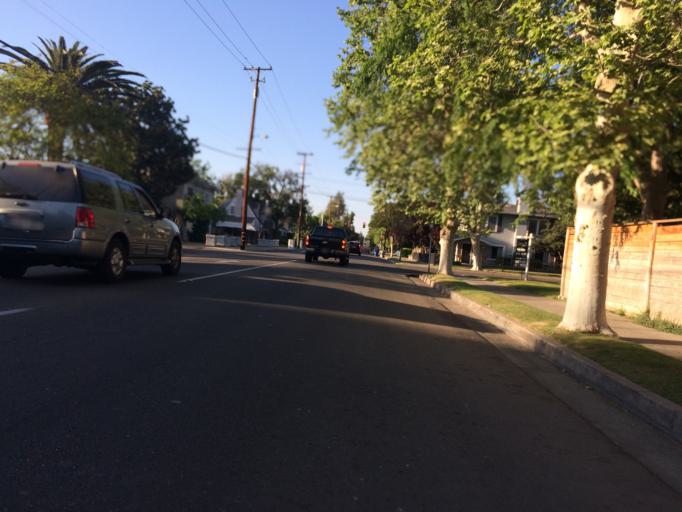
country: US
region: California
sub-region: Fresno County
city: Fresno
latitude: 36.7709
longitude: -119.7995
